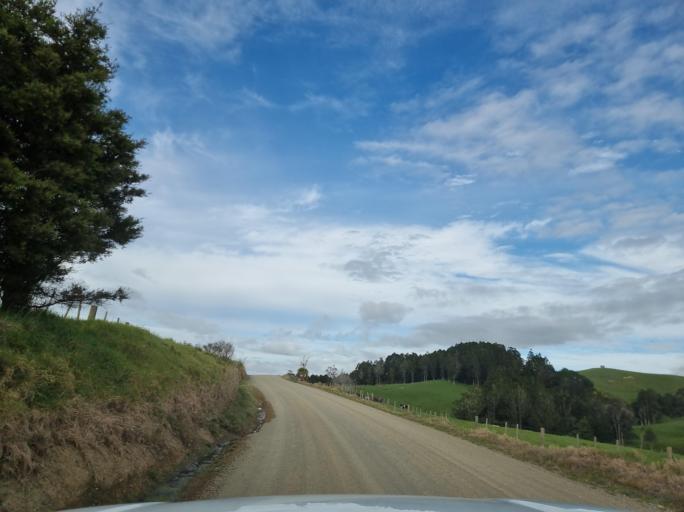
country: NZ
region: Northland
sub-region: Whangarei
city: Ruakaka
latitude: -36.0791
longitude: 174.3703
